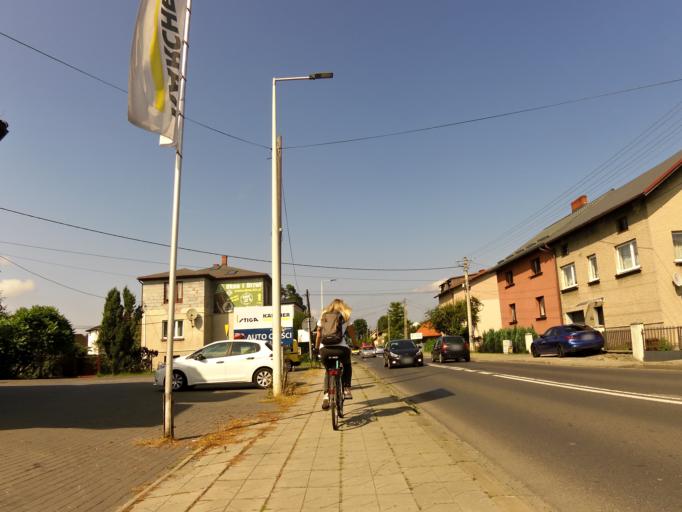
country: PL
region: Silesian Voivodeship
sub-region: Powiat zywiecki
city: Zywiec
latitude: 49.6701
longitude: 19.1802
